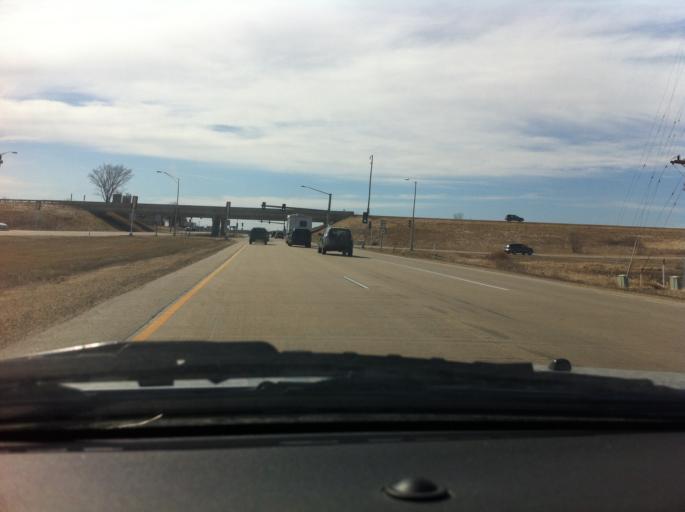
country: US
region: Wisconsin
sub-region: Dane County
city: Windsor
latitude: 43.1949
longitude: -89.3220
